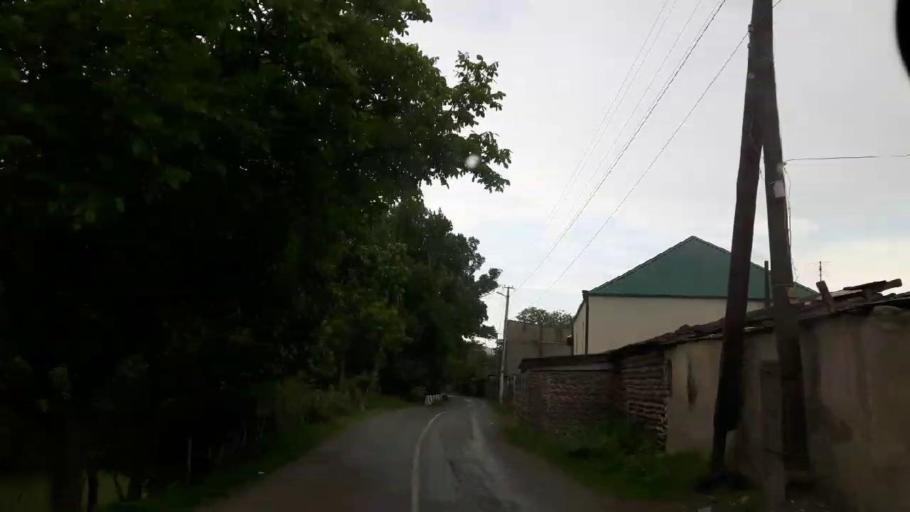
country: GE
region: Shida Kartli
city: Gori
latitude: 41.9641
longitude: 44.2201
